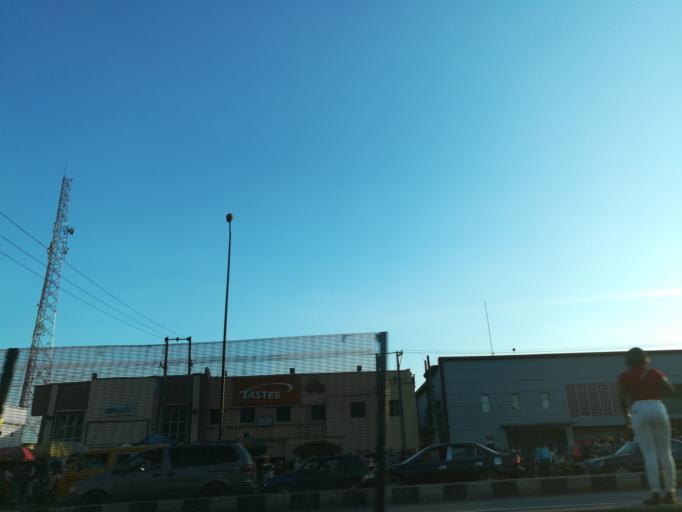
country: NG
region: Lagos
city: Ikorodu
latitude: 6.6228
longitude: 3.4982
